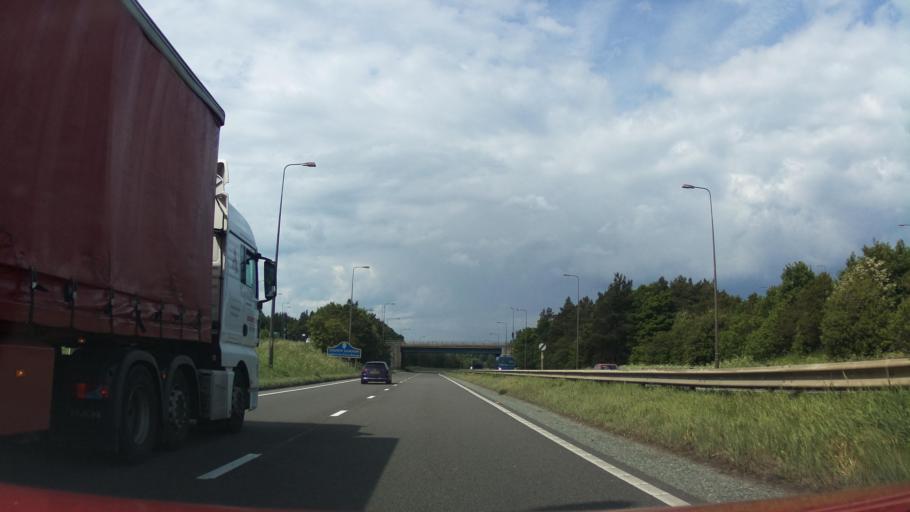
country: GB
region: England
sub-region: Hartlepool
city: Elwick
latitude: 54.6999
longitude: -1.3142
